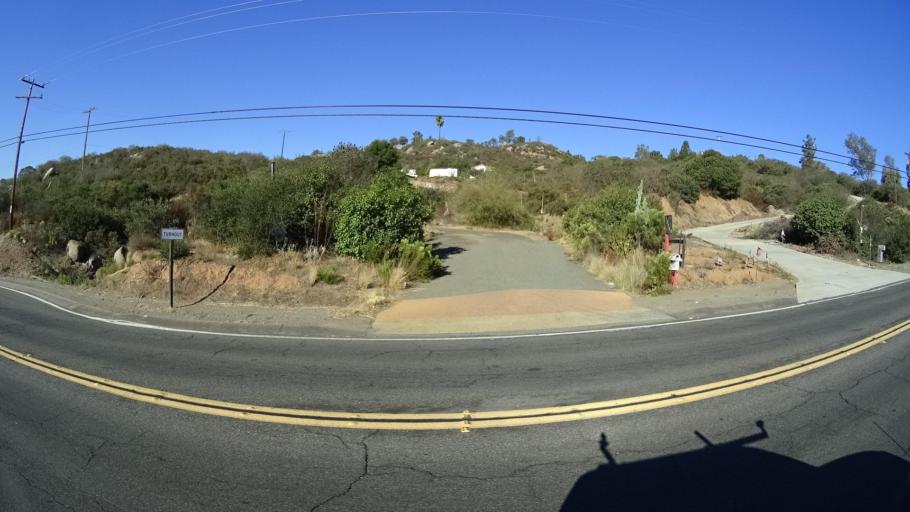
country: US
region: California
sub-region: San Diego County
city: Lakeside
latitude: 32.9094
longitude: -116.8841
